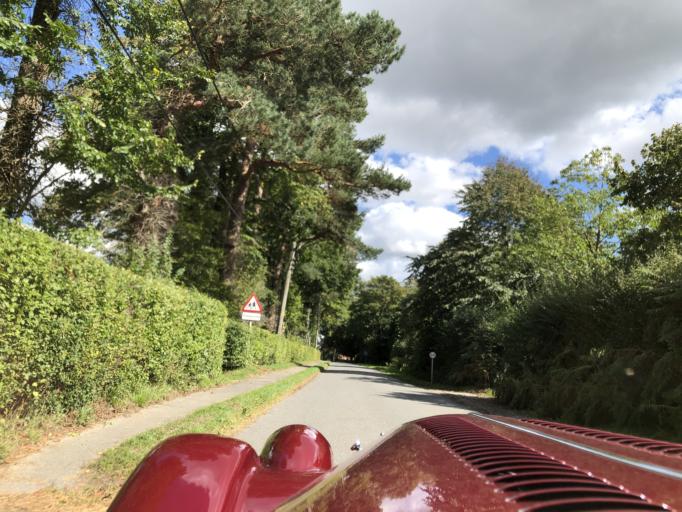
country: GB
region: England
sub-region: East Sussex
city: Northiam
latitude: 50.9909
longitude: 0.5513
